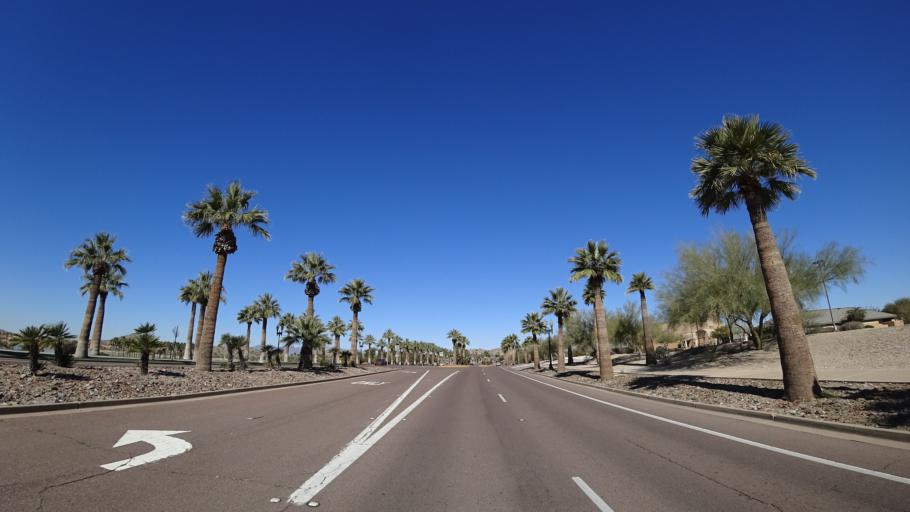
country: US
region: Arizona
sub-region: Maricopa County
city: Goodyear
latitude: 33.3503
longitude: -112.4282
